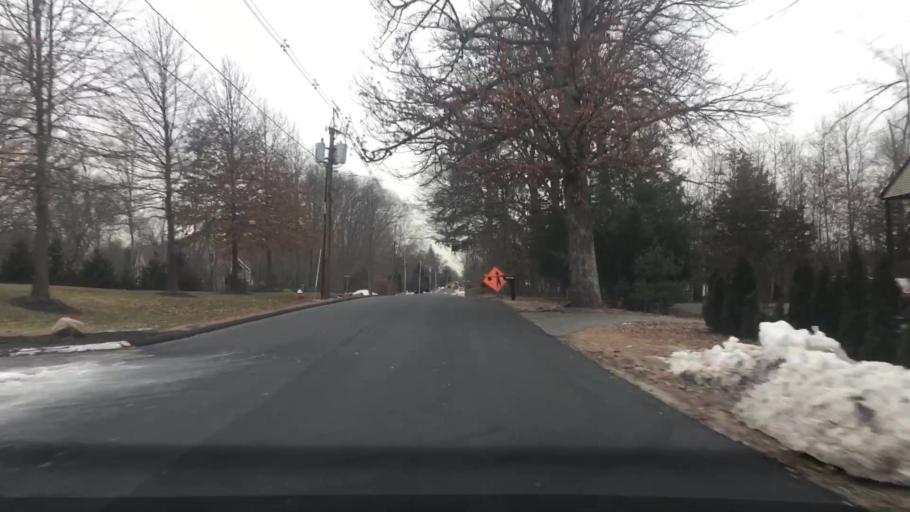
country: US
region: Connecticut
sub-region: Hartford County
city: Kensington
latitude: 41.6209
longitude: -72.7663
